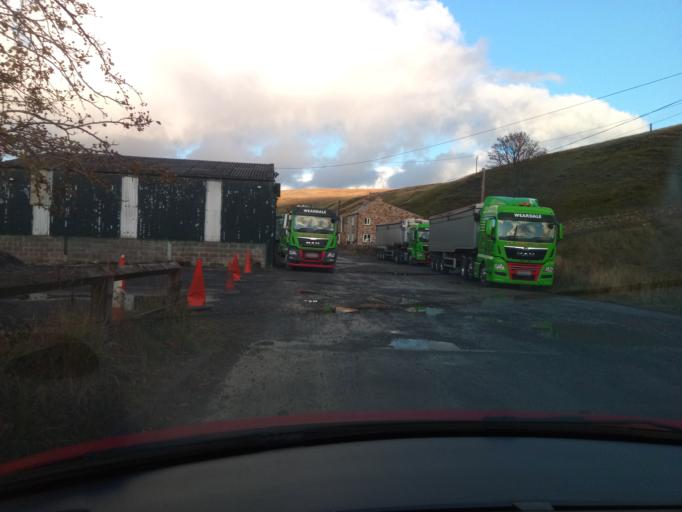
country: GB
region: England
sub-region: County Durham
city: Newbiggin
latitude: 54.7606
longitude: -2.2245
